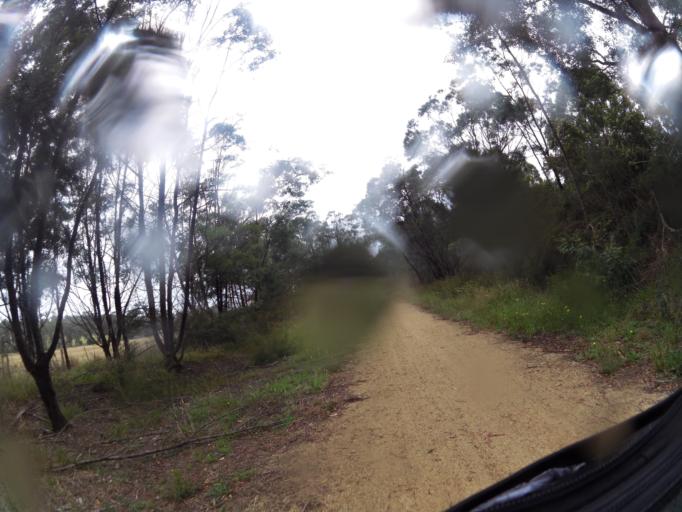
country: AU
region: Victoria
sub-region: East Gippsland
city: Bairnsdale
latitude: -37.7476
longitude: 147.8109
